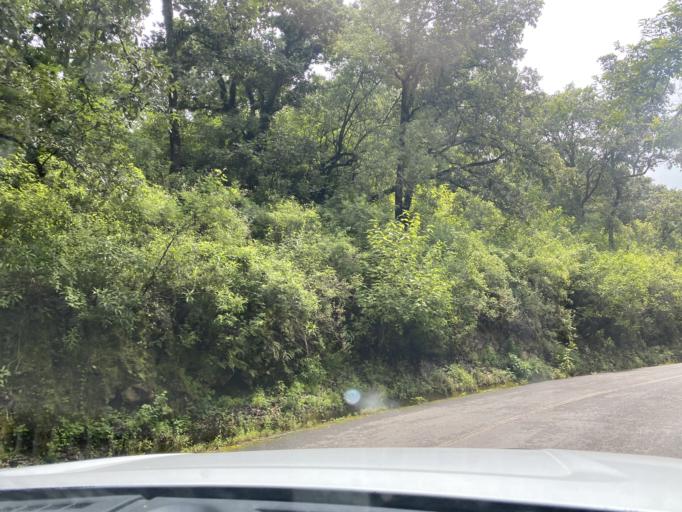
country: MX
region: Morelos
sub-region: Yecapixtla
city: Achichipico
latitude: 18.9399
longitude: -98.8227
